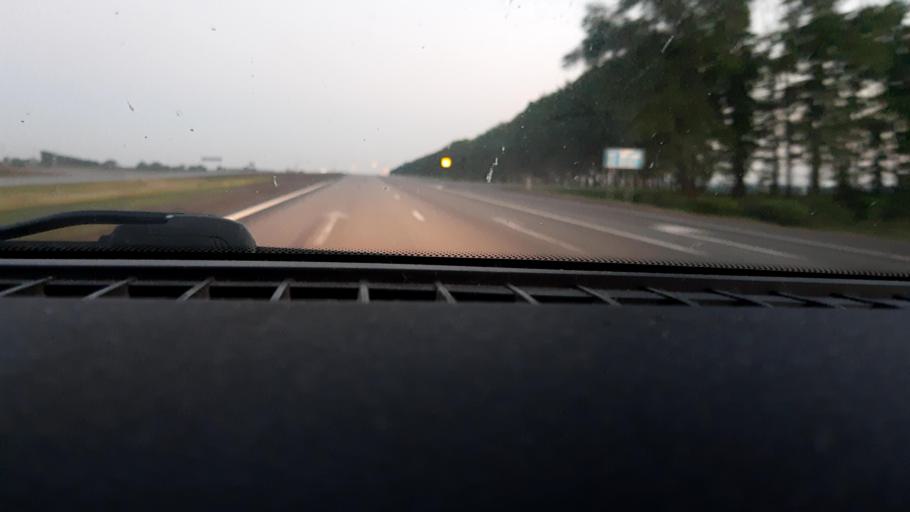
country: RU
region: Bashkortostan
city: Chishmy
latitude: 54.6552
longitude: 55.4893
